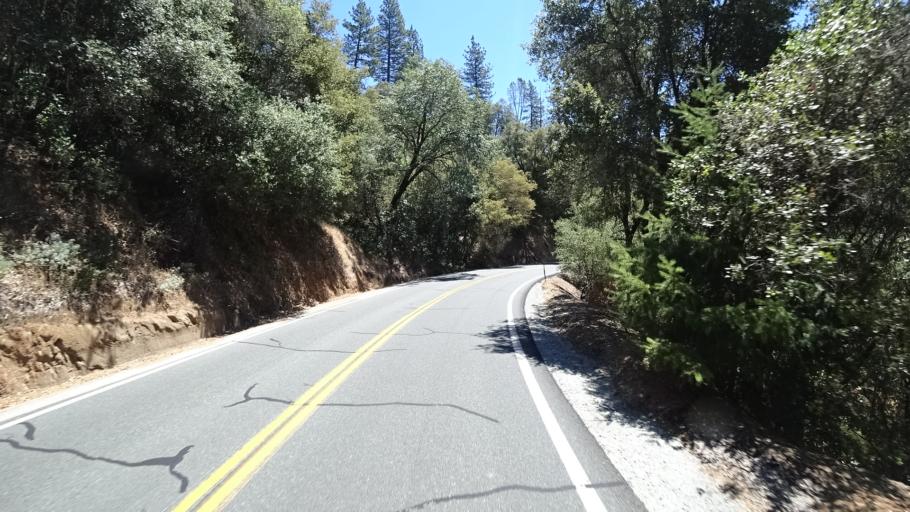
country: US
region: California
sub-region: Amador County
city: Pioneer
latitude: 38.3700
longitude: -120.5502
